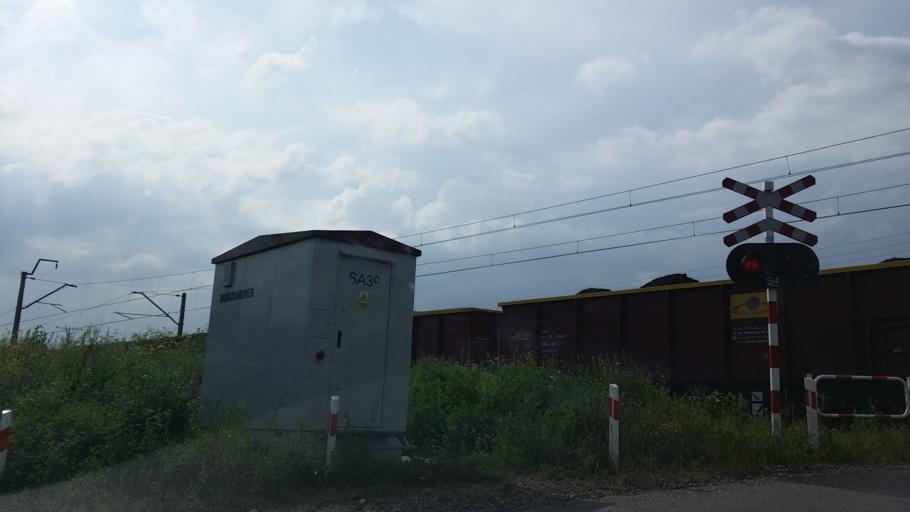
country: PL
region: Lesser Poland Voivodeship
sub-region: Powiat wadowicki
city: Spytkowice
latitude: 50.0007
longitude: 19.5117
